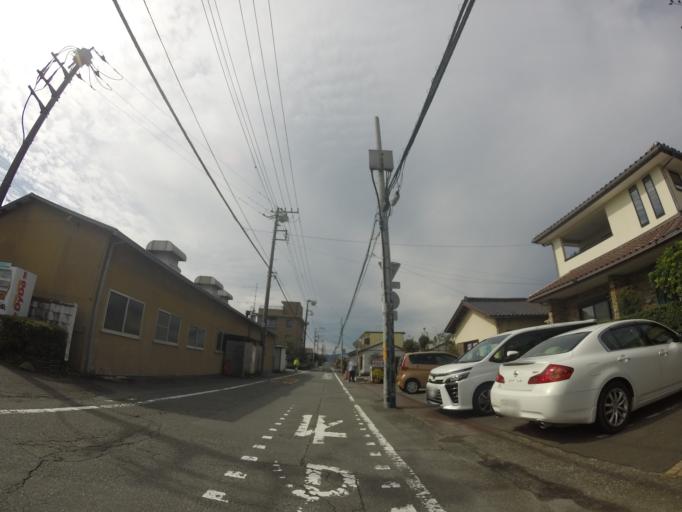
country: JP
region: Shizuoka
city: Fuji
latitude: 35.1350
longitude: 138.6500
